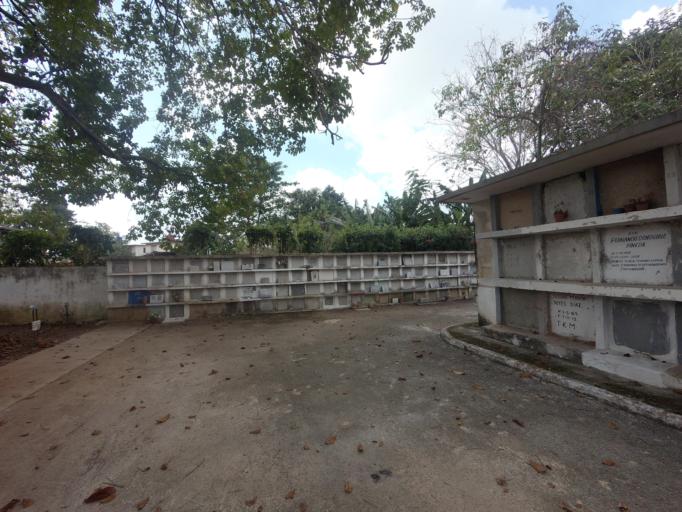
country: CU
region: Artemisa
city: Bauta
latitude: 22.9822
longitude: -82.5523
